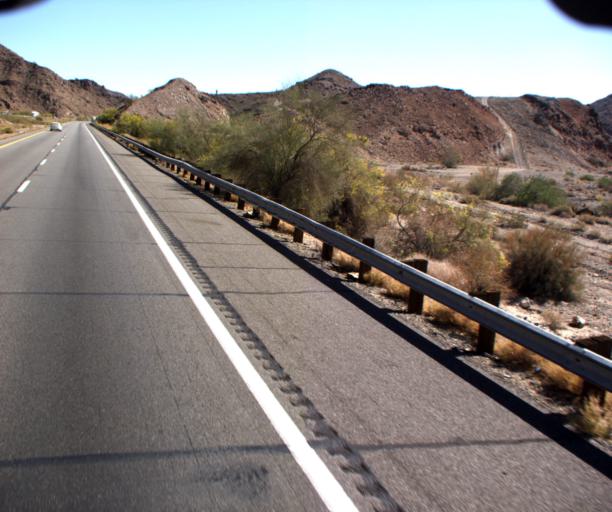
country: US
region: Arizona
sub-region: La Paz County
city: Quartzsite
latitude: 33.6450
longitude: -114.3790
